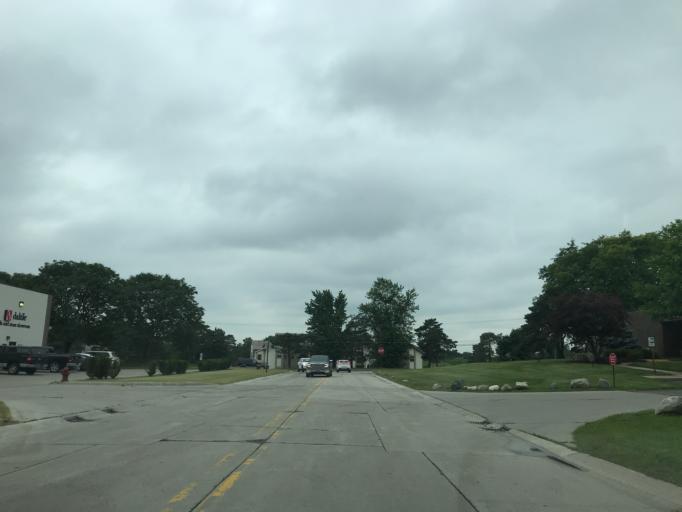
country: US
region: Michigan
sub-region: Oakland County
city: Farmington
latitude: 42.4725
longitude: -83.3952
